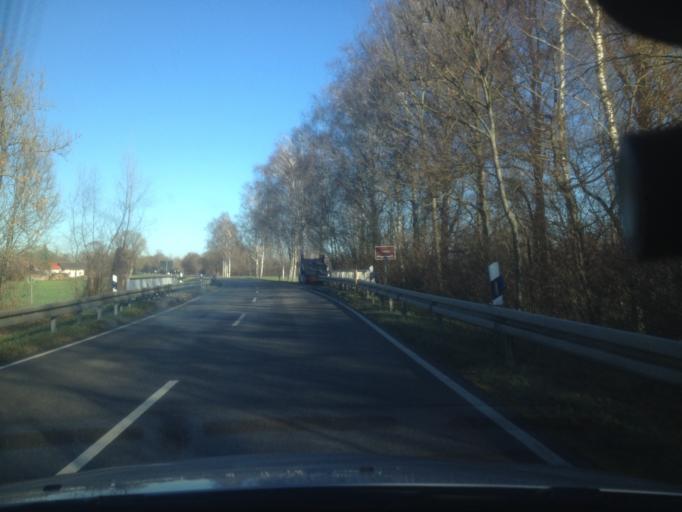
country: DE
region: Bavaria
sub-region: Upper Bavaria
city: Berglern
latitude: 48.4168
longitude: 11.9334
